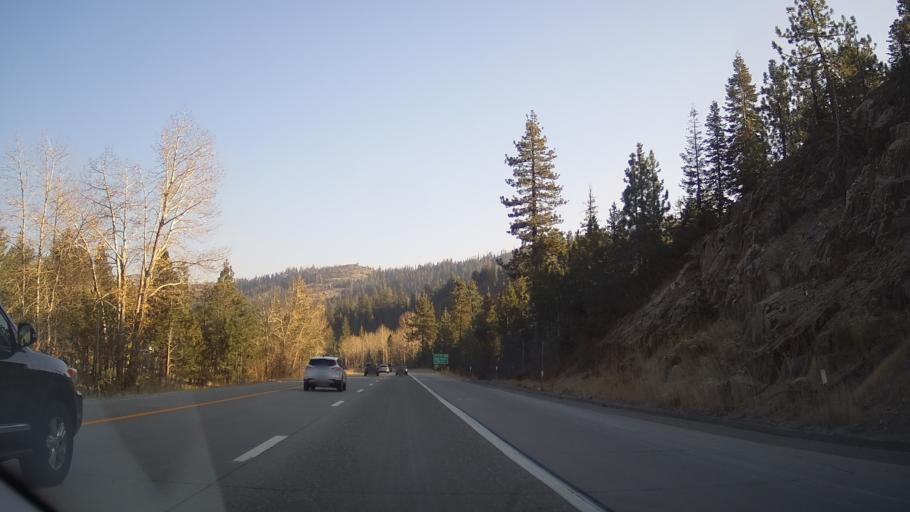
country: US
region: California
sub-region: Nevada County
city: Truckee
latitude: 39.3075
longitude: -120.5407
